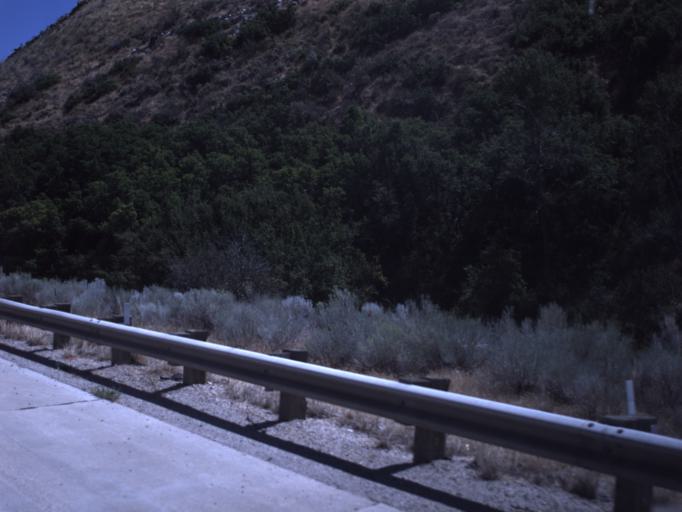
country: US
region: Utah
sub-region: Morgan County
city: Morgan
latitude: 41.0616
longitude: -111.5717
